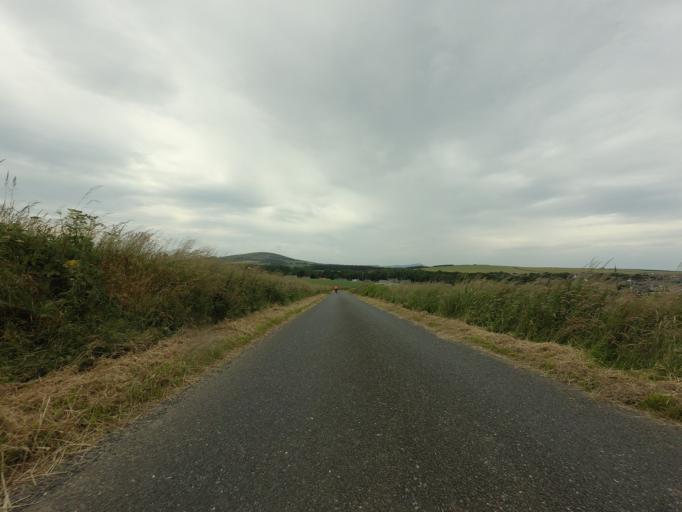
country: GB
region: Scotland
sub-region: Aberdeenshire
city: Portsoy
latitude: 57.6783
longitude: -2.6822
